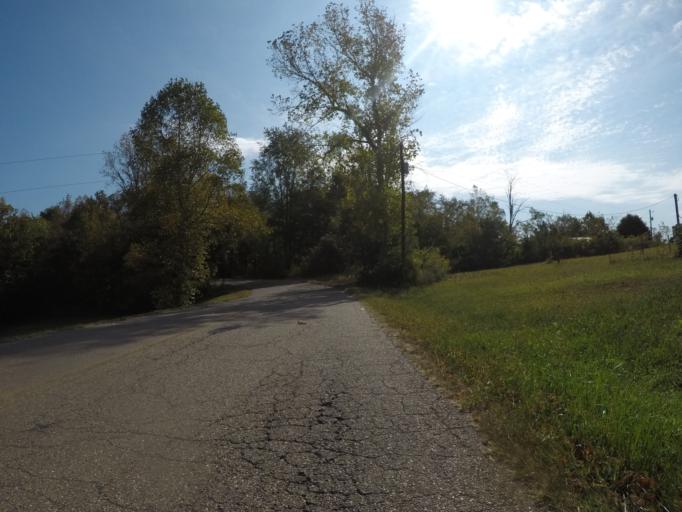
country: US
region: West Virginia
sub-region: Cabell County
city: Lesage
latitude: 38.5957
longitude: -82.4175
